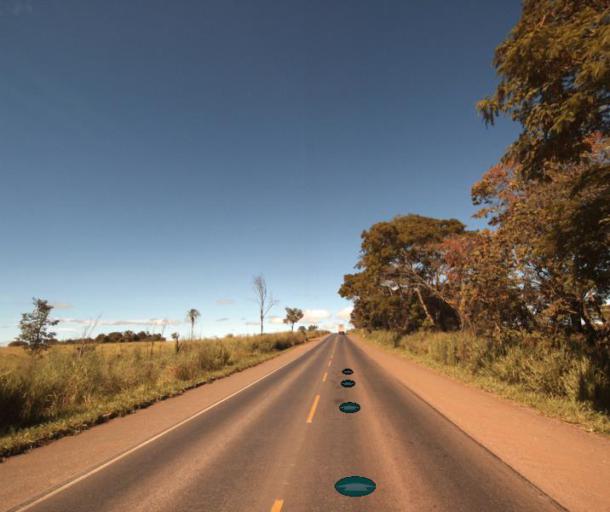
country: BR
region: Goias
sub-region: Itapaci
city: Itapaci
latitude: -15.0499
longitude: -49.4448
